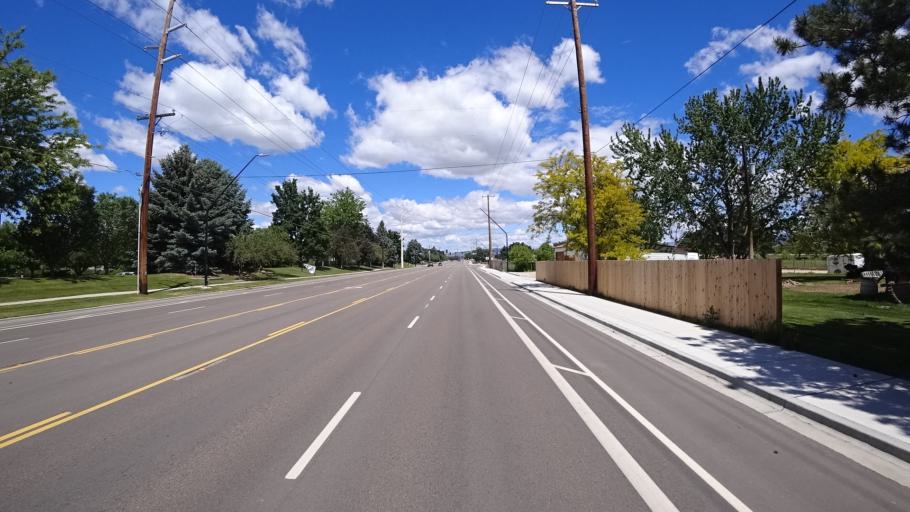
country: US
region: Idaho
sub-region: Ada County
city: Eagle
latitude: 43.6579
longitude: -116.3343
